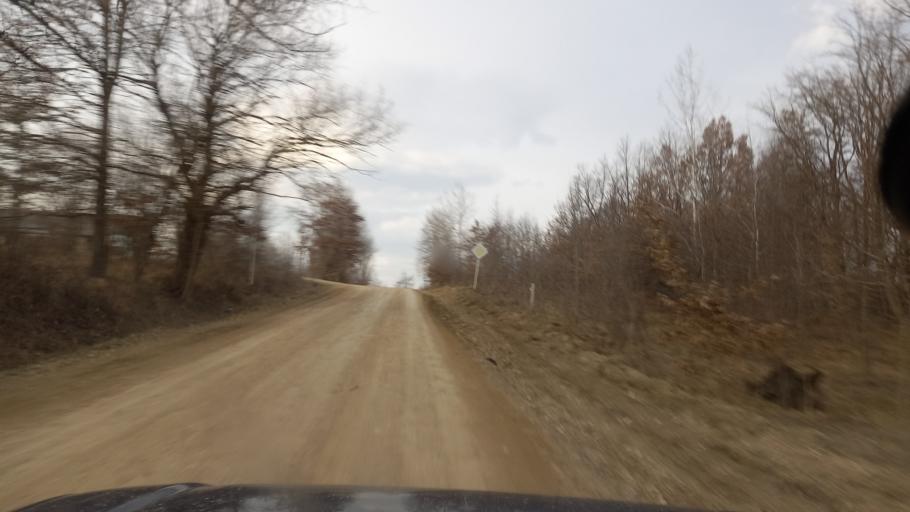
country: RU
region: Adygeya
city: Kamennomostskiy
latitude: 44.1679
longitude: 40.2468
